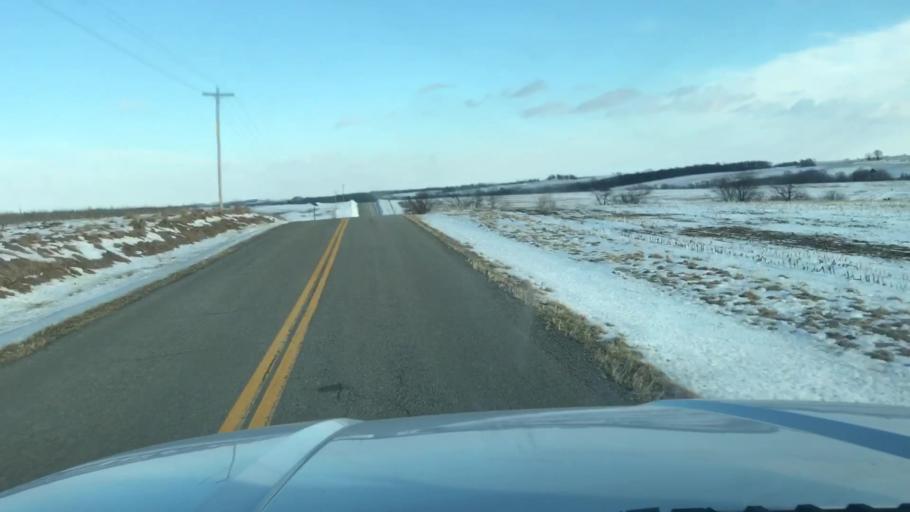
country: US
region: Missouri
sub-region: Holt County
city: Oregon
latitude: 40.1006
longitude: -94.9895
